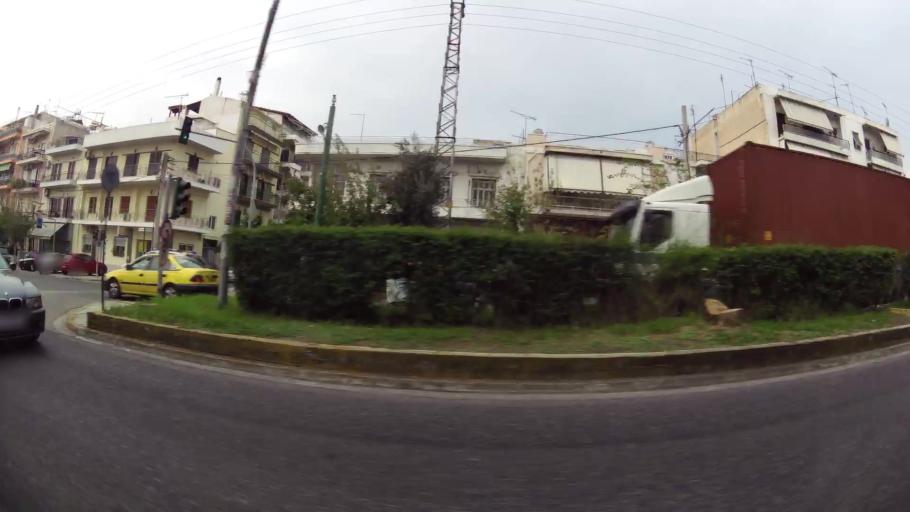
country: GR
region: Attica
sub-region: Nomarchia Athinas
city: Agia Varvara
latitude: 37.9798
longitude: 23.6576
